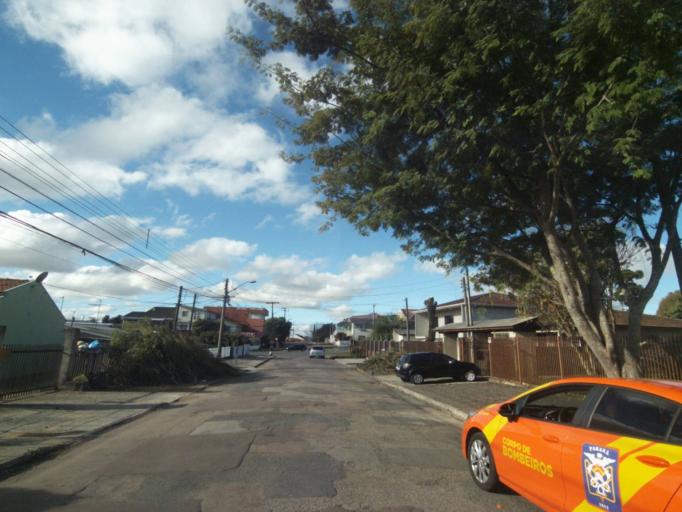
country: BR
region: Parana
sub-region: Sao Jose Dos Pinhais
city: Sao Jose dos Pinhais
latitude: -25.5280
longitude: -49.2905
